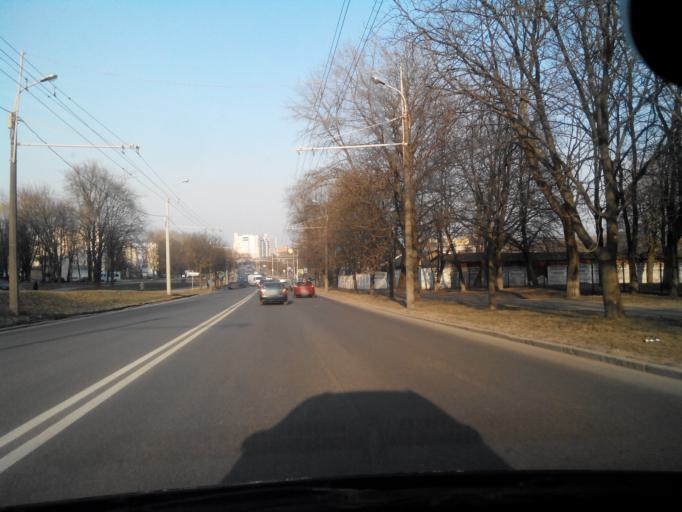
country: BY
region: Minsk
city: Novoye Medvezhino
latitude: 53.8964
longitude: 27.5025
